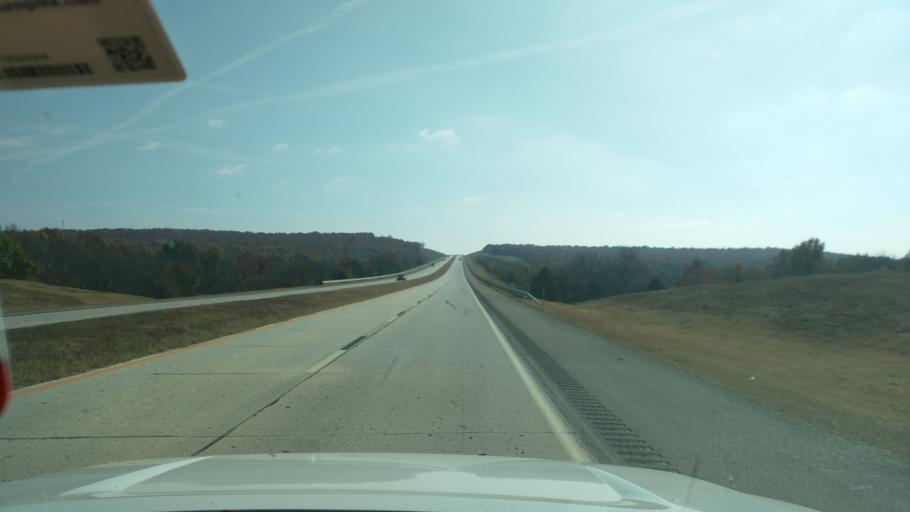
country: US
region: Oklahoma
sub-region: Muskogee County
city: Warner
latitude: 35.5526
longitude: -95.2348
